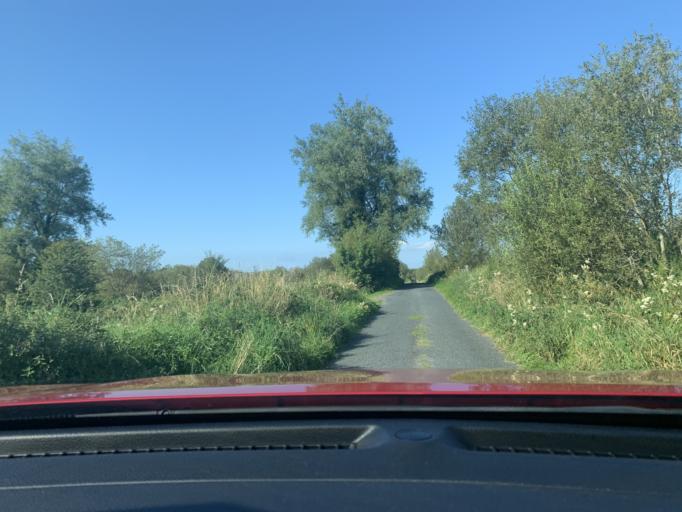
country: IE
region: Connaught
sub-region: Sligo
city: Tobercurry
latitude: 54.0656
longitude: -8.7805
